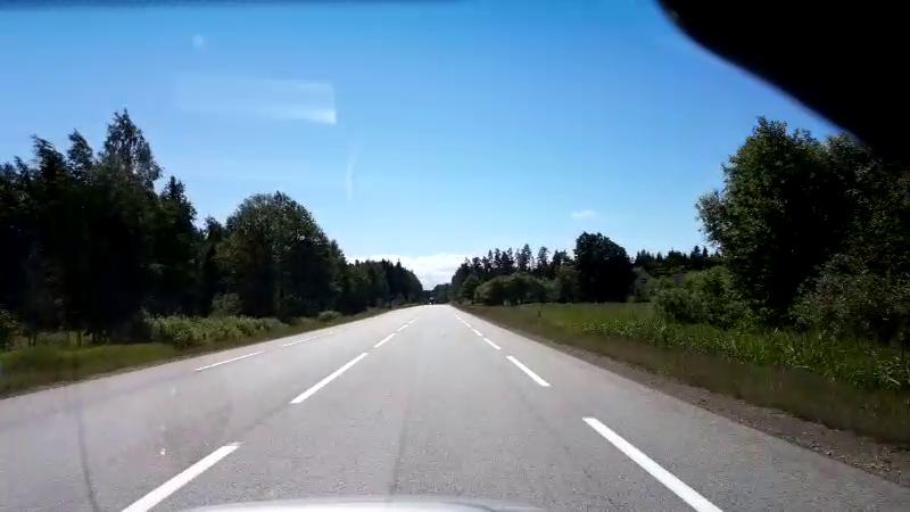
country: LV
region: Saulkrastu
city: Saulkrasti
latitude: 57.4246
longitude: 24.4291
